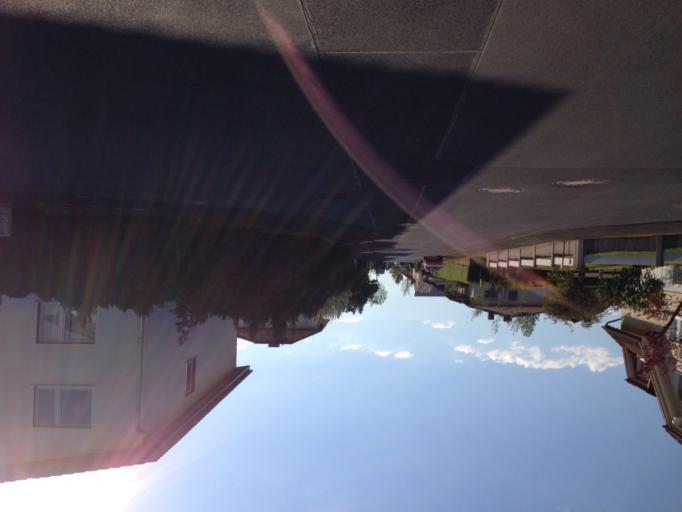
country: DE
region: Hesse
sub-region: Regierungsbezirk Giessen
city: Lich
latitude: 50.5523
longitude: 8.7847
